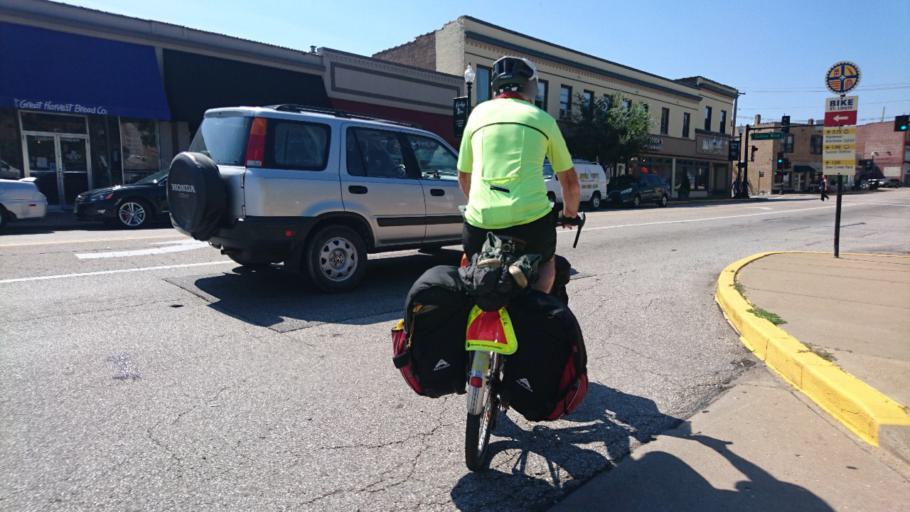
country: US
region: Missouri
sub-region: Saint Louis County
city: Maplewood
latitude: 38.6128
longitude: -90.3191
